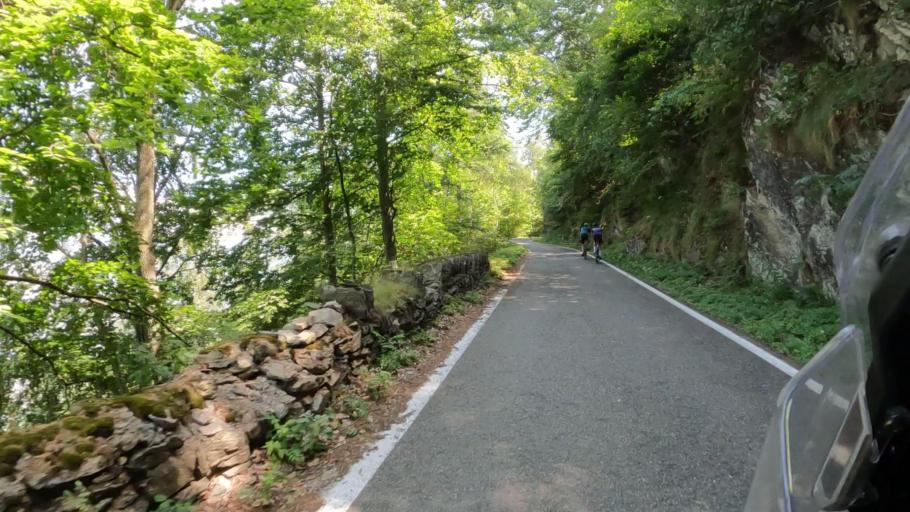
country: IT
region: Piedmont
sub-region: Provincia di Torino
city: Meana di Susa
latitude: 45.1080
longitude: 7.0692
